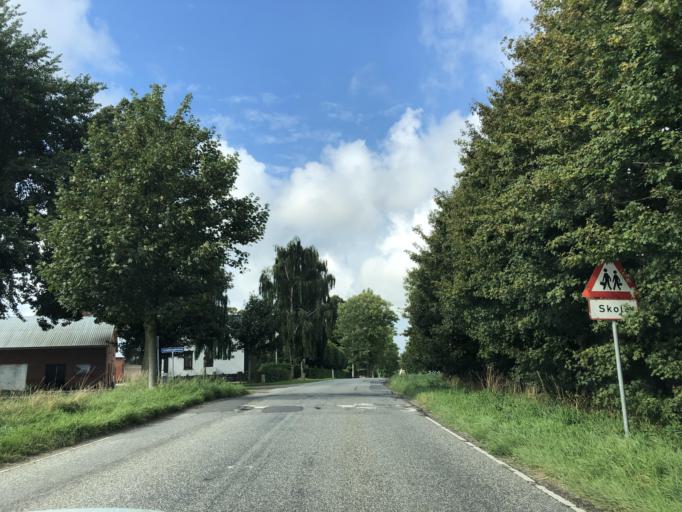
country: DK
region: North Denmark
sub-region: Alborg Kommune
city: Nibe
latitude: 56.9655
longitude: 9.6870
